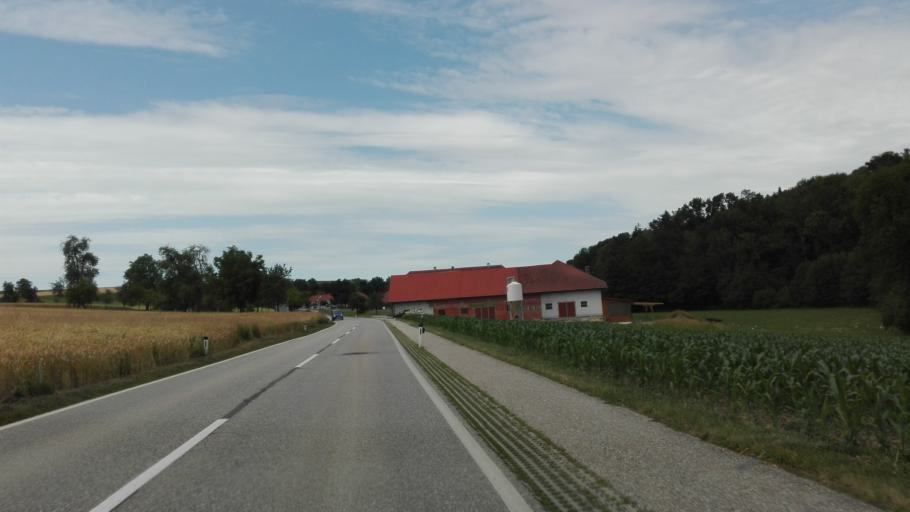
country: AT
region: Upper Austria
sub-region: Politischer Bezirk Grieskirchen
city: Grieskirchen
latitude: 48.2531
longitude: 13.8125
